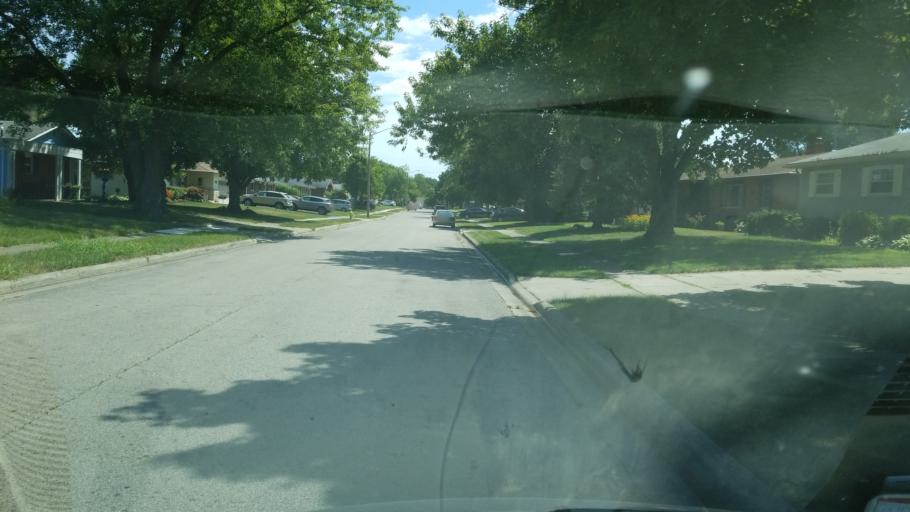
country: US
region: Ohio
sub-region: Franklin County
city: Grove City
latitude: 39.8763
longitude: -83.0744
